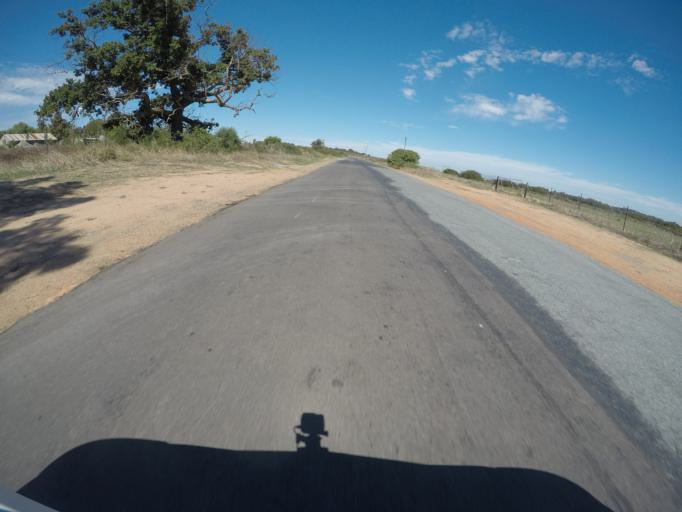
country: ZA
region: Western Cape
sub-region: West Coast District Municipality
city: Malmesbury
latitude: -33.5866
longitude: 18.6467
